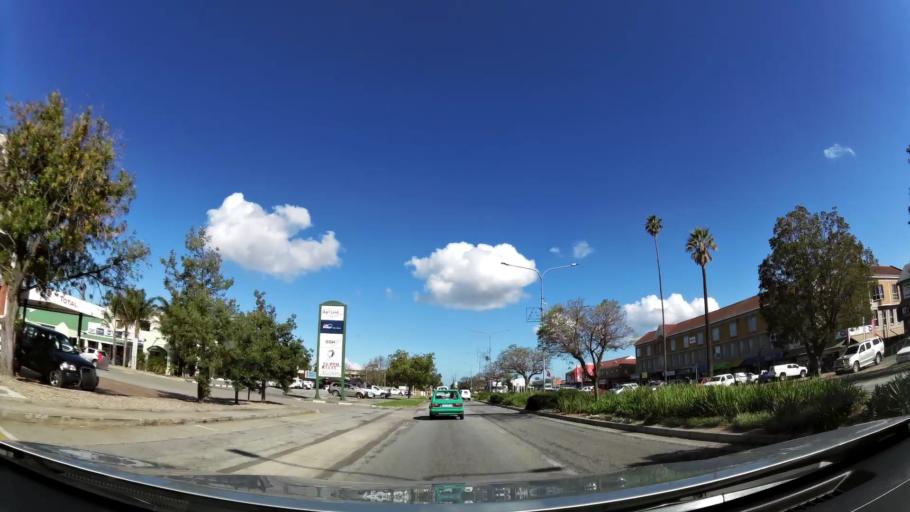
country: ZA
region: Western Cape
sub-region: Eden District Municipality
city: George
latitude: -33.9627
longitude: 22.4538
